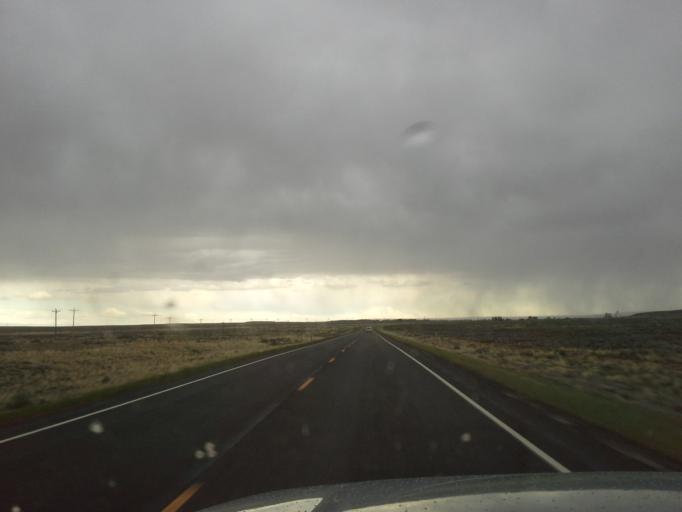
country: US
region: Wyoming
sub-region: Park County
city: Powell
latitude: 45.0281
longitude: -108.6359
